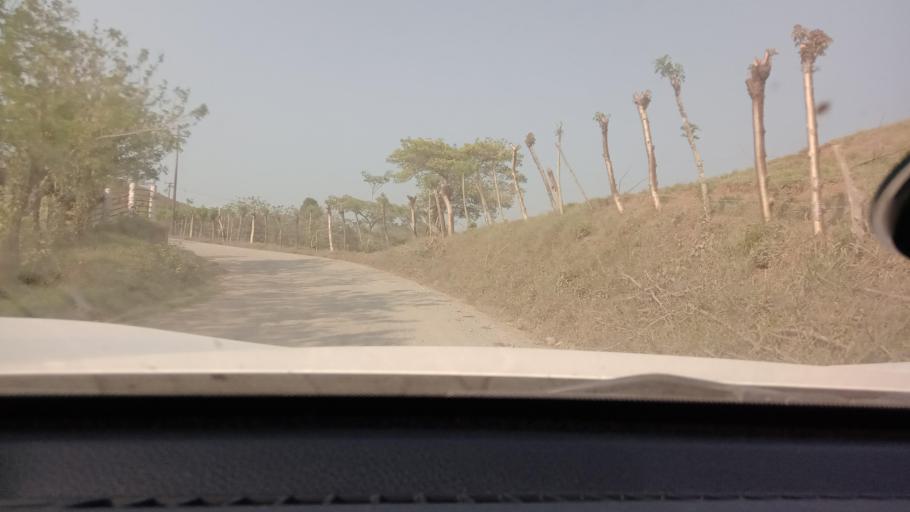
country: MX
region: Tabasco
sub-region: Huimanguillo
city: Francisco Rueda
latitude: 17.6506
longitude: -93.9015
